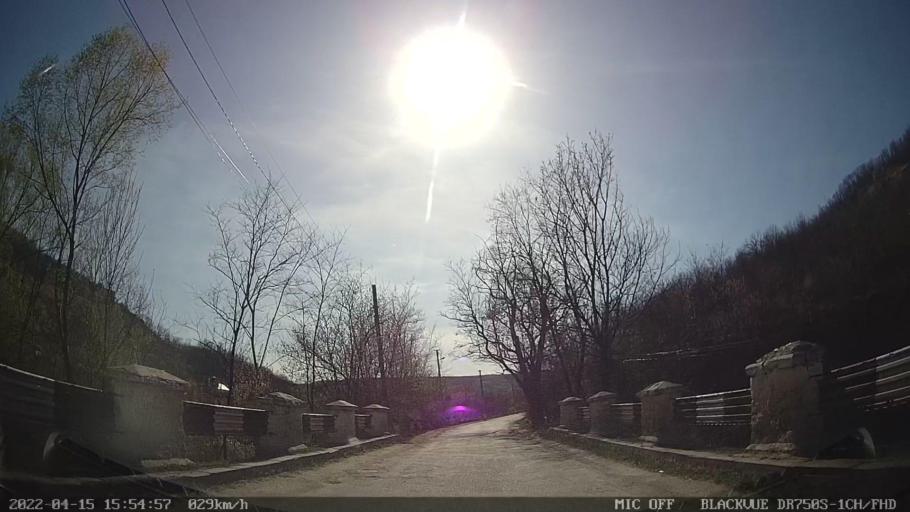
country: MD
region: Raionul Ocnita
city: Otaci
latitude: 48.4020
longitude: 27.8876
